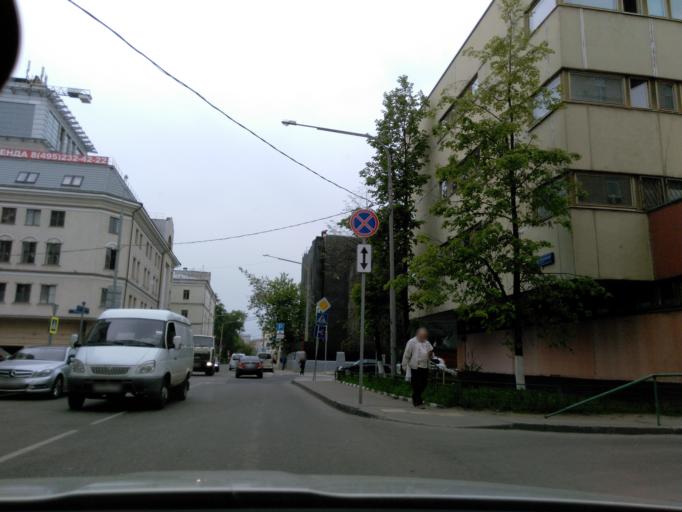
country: RU
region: Moscow
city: Zamoskvorech'ye
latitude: 55.7298
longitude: 37.6301
